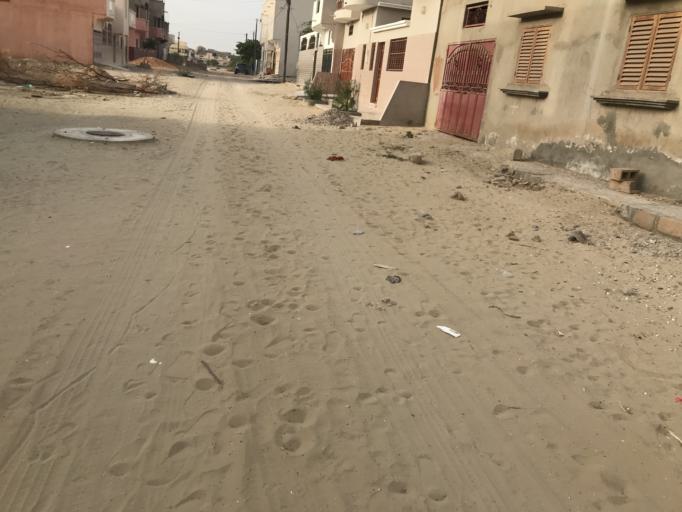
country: SN
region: Saint-Louis
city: Saint-Louis
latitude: 16.0360
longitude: -16.4455
